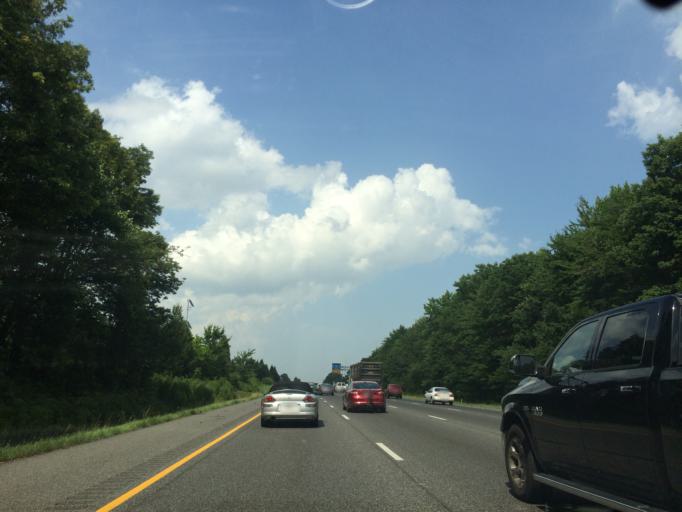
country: US
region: Maryland
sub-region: Howard County
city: Savage
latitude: 39.1617
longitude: -76.8170
